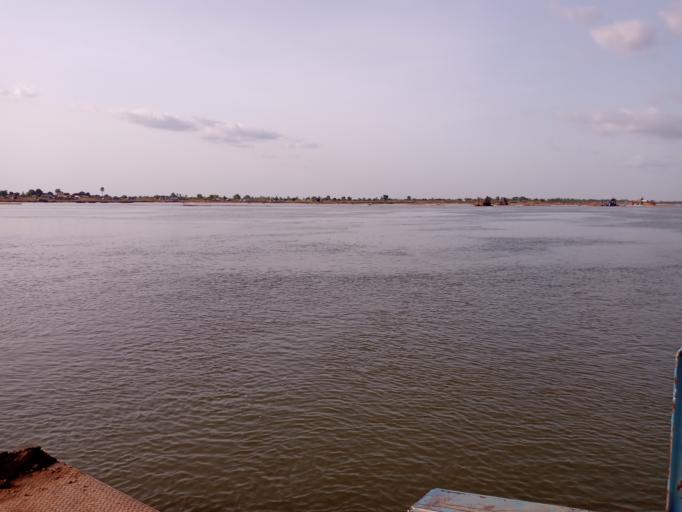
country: ML
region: Koulikoro
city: Kangaba
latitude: 12.1610
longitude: -8.2434
